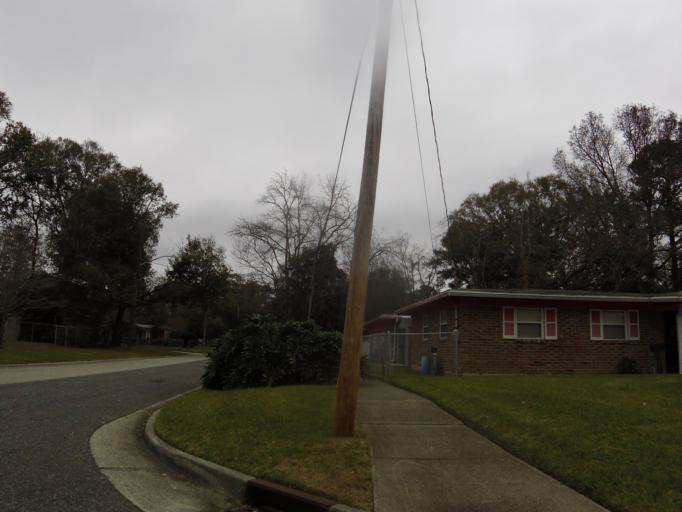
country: US
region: Florida
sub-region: Duval County
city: Jacksonville
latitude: 30.3611
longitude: -81.7066
